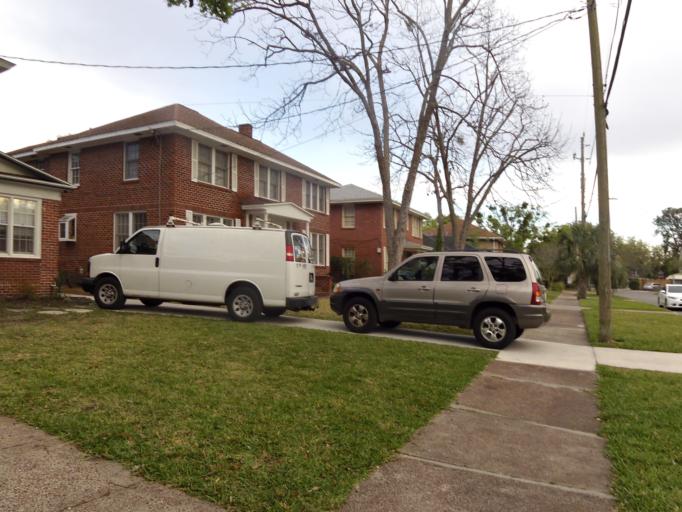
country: US
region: Florida
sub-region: Duval County
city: Jacksonville
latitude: 30.3066
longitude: -81.6579
